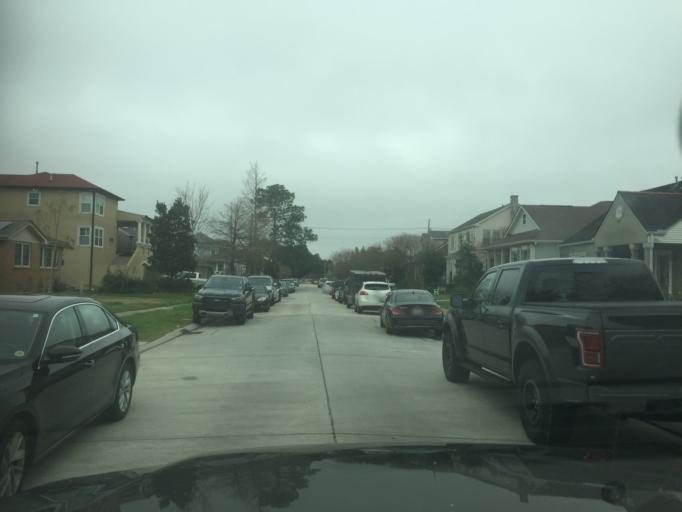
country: US
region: Louisiana
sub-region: Jefferson Parish
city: Metairie
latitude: 30.0060
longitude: -90.1091
